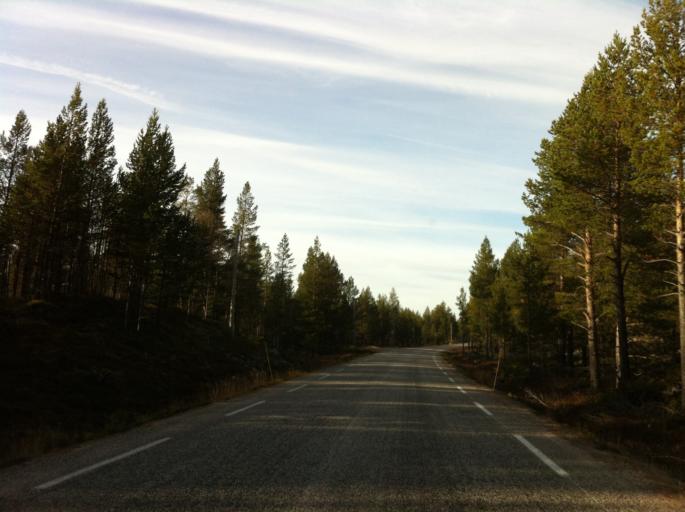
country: NO
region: Hedmark
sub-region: Engerdal
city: Engerdal
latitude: 62.1238
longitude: 12.0033
